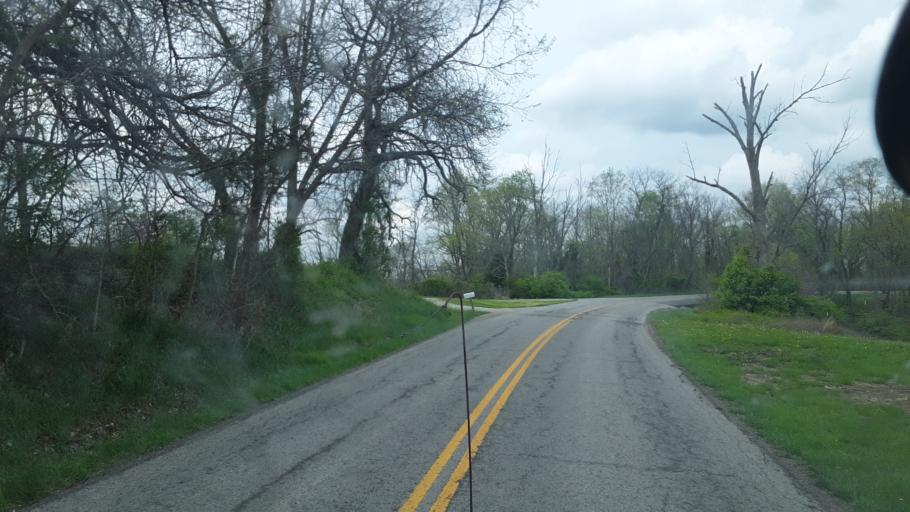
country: US
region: Kentucky
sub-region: Grant County
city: Dry Ridge
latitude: 38.6557
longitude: -84.7028
